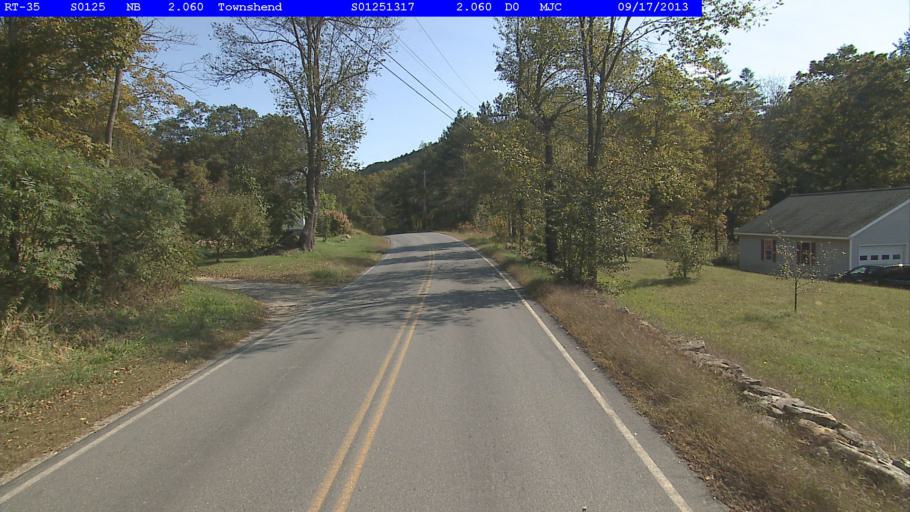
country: US
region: Vermont
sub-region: Windham County
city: Newfane
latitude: 43.0715
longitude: -72.6522
